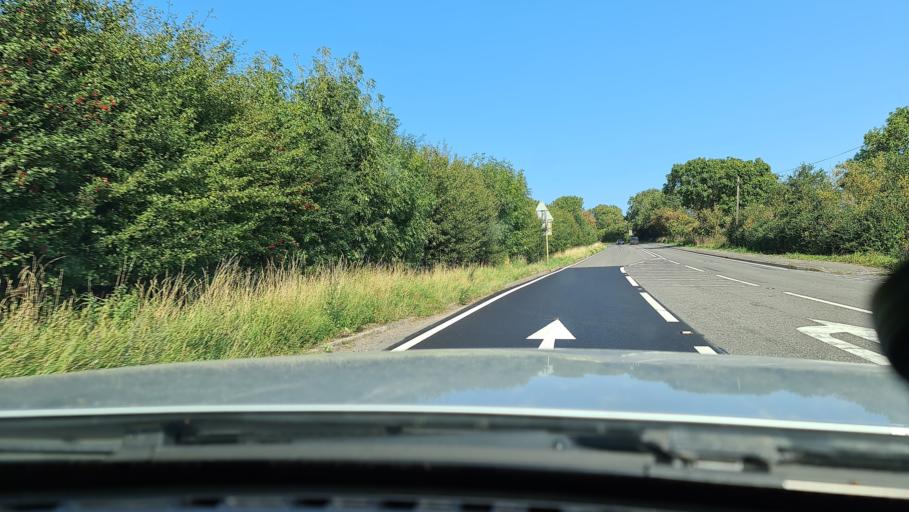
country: GB
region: England
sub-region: Northamptonshire
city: Bugbrooke
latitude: 52.1984
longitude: -1.0404
